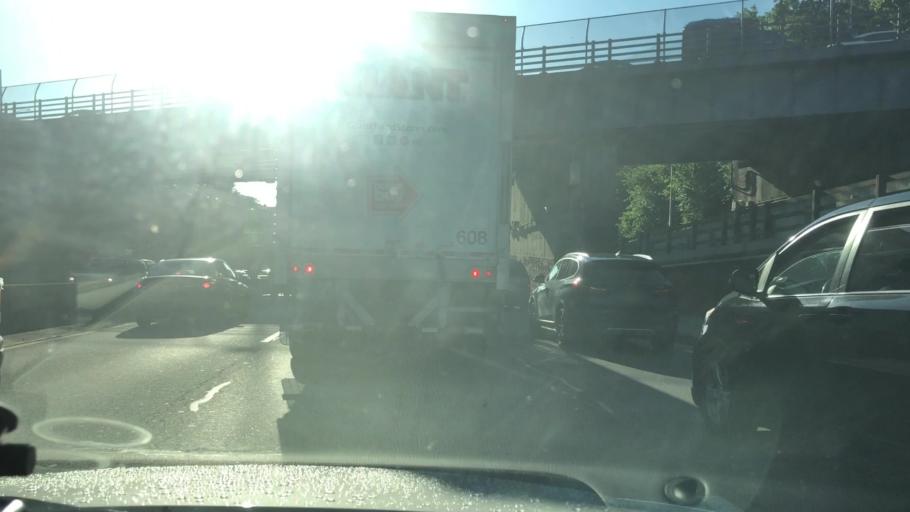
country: US
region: New York
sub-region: New York County
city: Inwood
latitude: 40.8446
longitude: -73.9210
